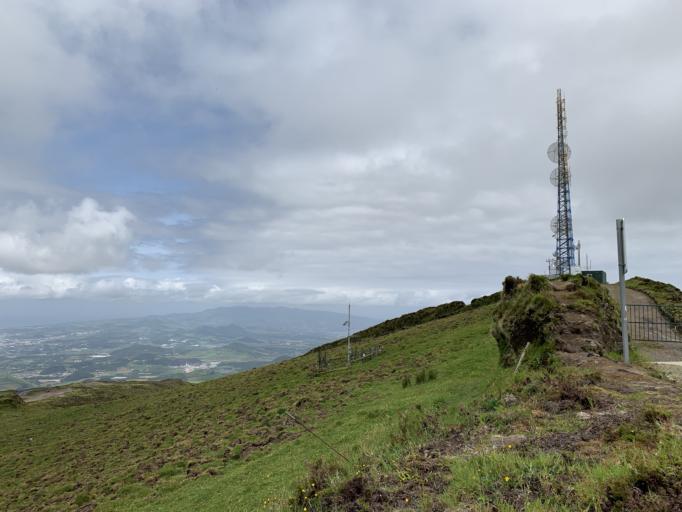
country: PT
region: Azores
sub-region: Vila Franca do Campo
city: Vila Franca do Campo
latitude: 37.7637
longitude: -25.4951
